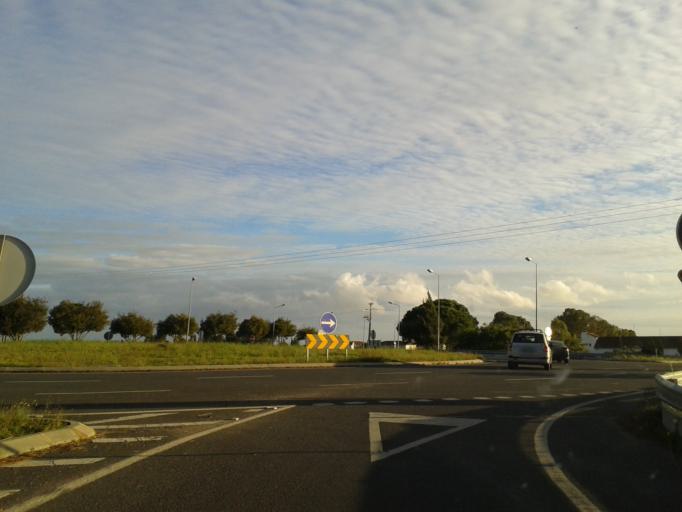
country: PT
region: Beja
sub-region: Beja
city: Beja
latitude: 38.0033
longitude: -7.8668
